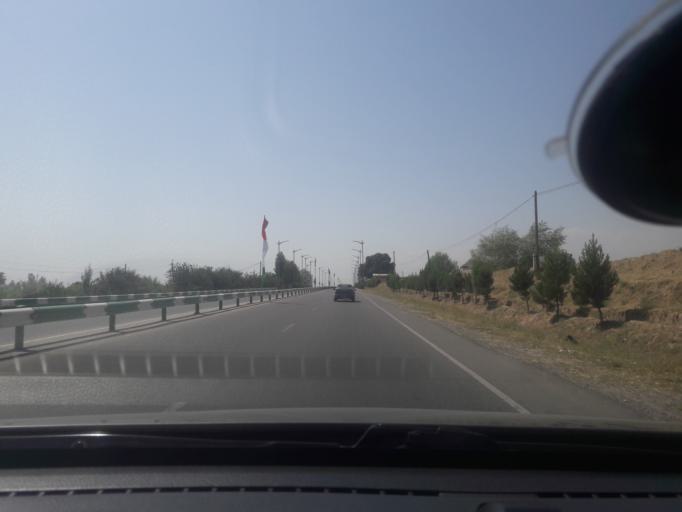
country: TJ
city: Shahrinav
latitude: 38.5612
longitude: 68.4416
